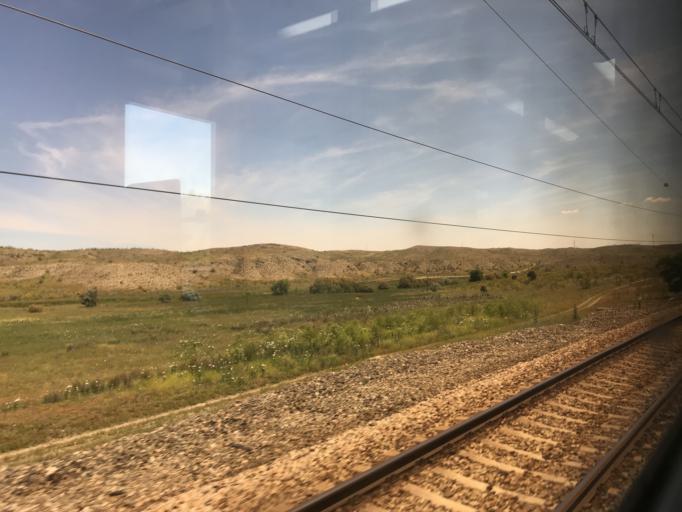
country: ES
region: Madrid
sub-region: Provincia de Madrid
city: Ciempozuelos
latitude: 40.1846
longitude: -3.6437
